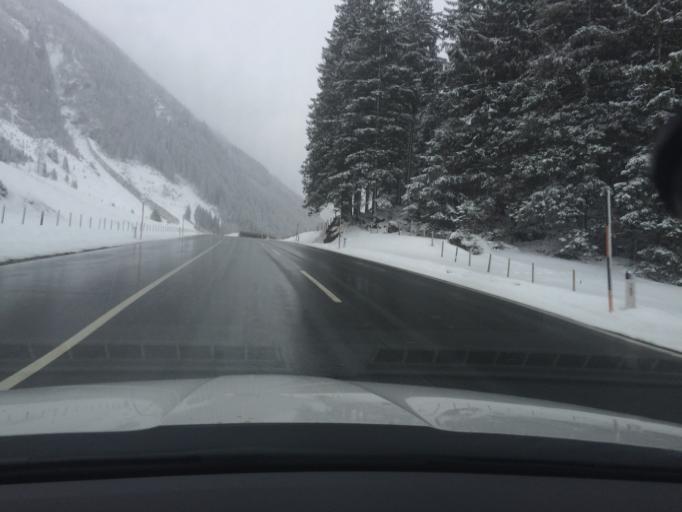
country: AT
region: Salzburg
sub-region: Politischer Bezirk Zell am See
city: Stuhlfelden
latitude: 47.1973
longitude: 12.5155
